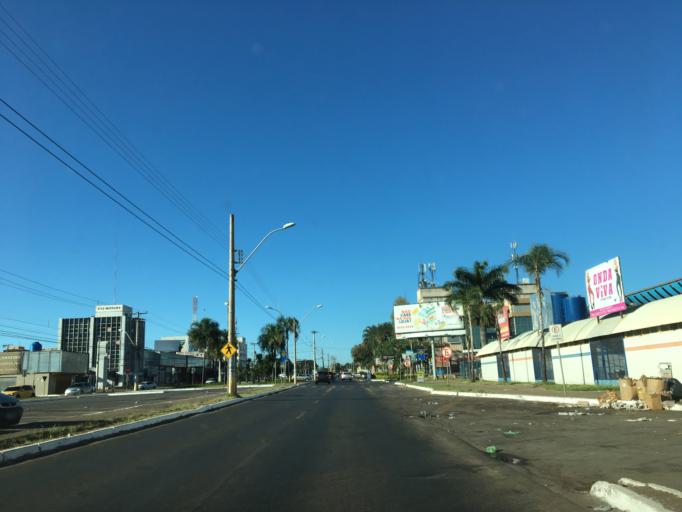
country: BR
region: Federal District
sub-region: Brasilia
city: Brasilia
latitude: -15.7967
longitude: -47.9493
